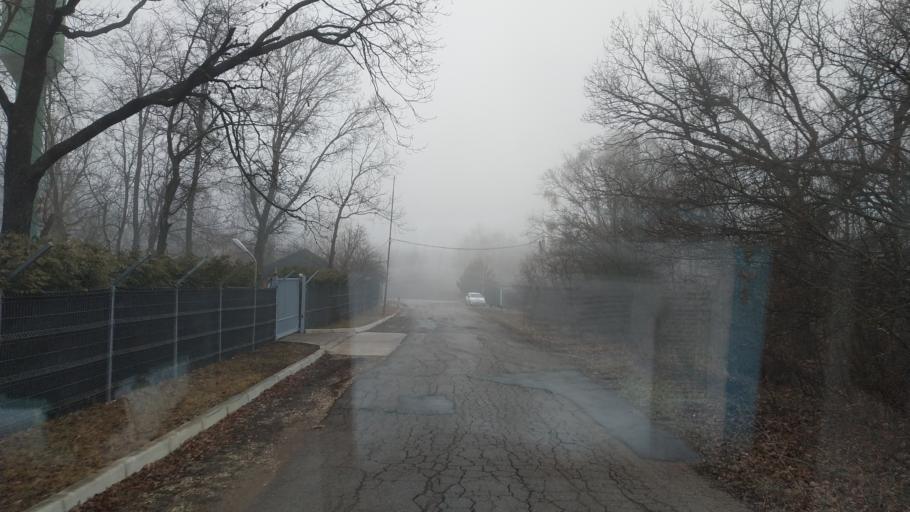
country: MD
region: Laloveni
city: Ialoveni
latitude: 46.9479
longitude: 28.6995
